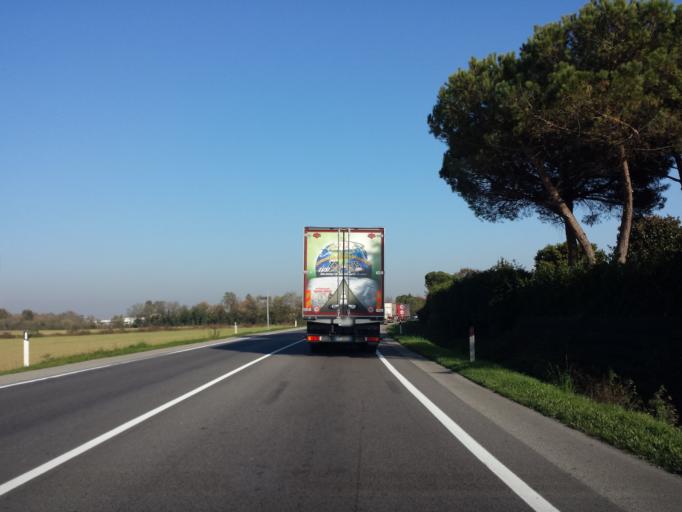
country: IT
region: Veneto
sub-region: Provincia di Treviso
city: Castelfranco Veneto
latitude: 45.6822
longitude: 11.9216
